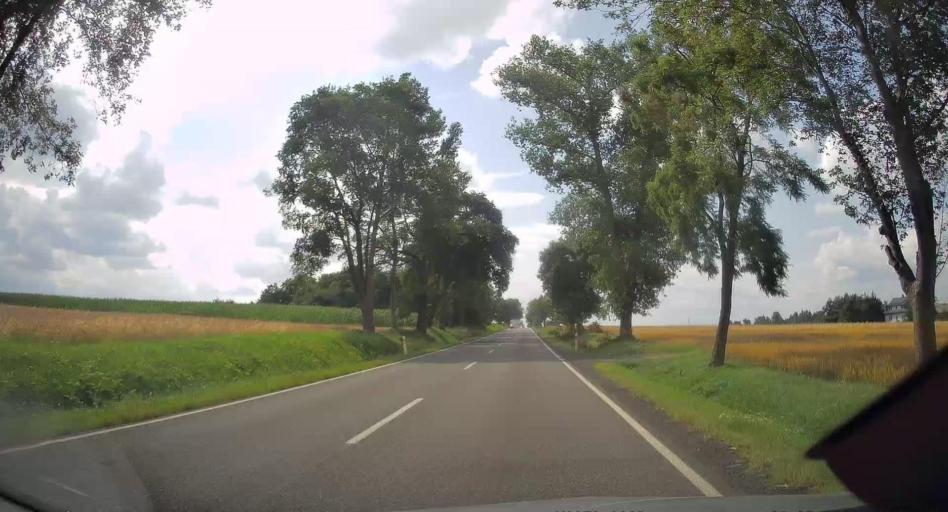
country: PL
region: Lodz Voivodeship
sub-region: Powiat brzezinski
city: Jezow
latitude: 51.8096
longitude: 20.0040
